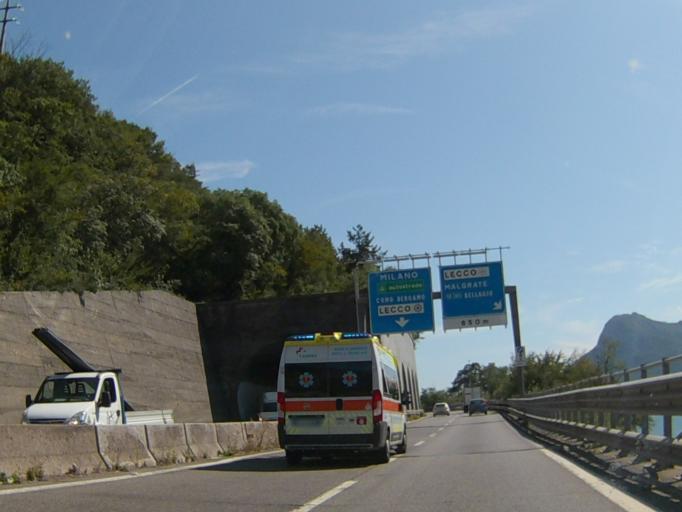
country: IT
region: Lombardy
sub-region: Provincia di Lecco
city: Abbadia Lariana
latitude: 45.8854
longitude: 9.3603
